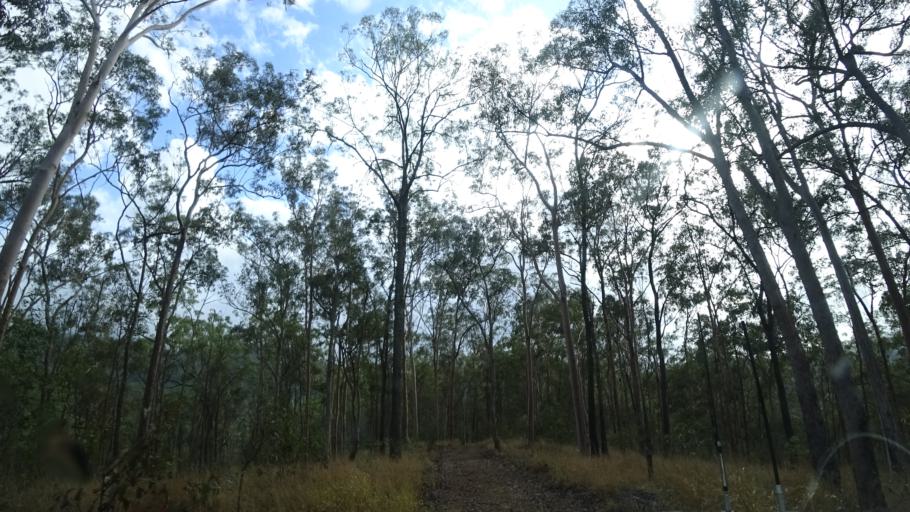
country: AU
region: Queensland
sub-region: Brisbane
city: Pullenvale
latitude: -27.4576
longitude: 152.8697
